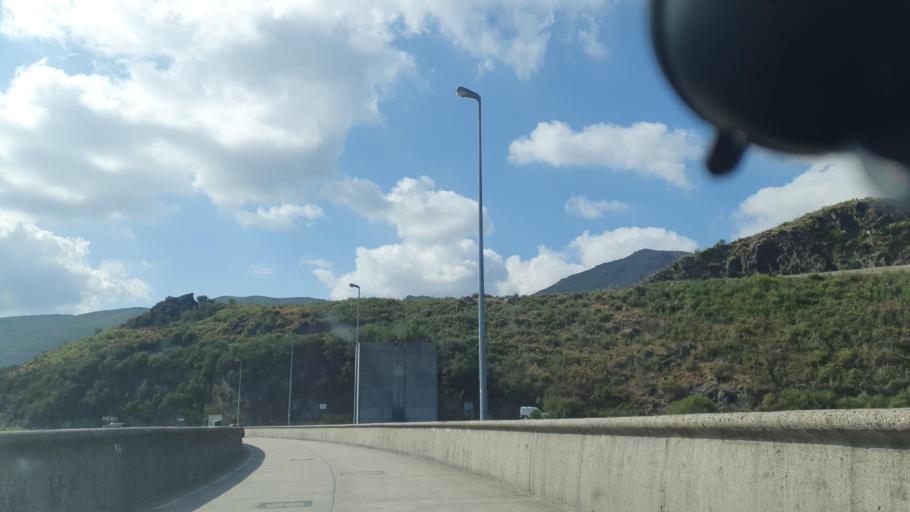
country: PT
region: Braga
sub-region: Terras de Bouro
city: Antas
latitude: 41.7640
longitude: -8.2095
